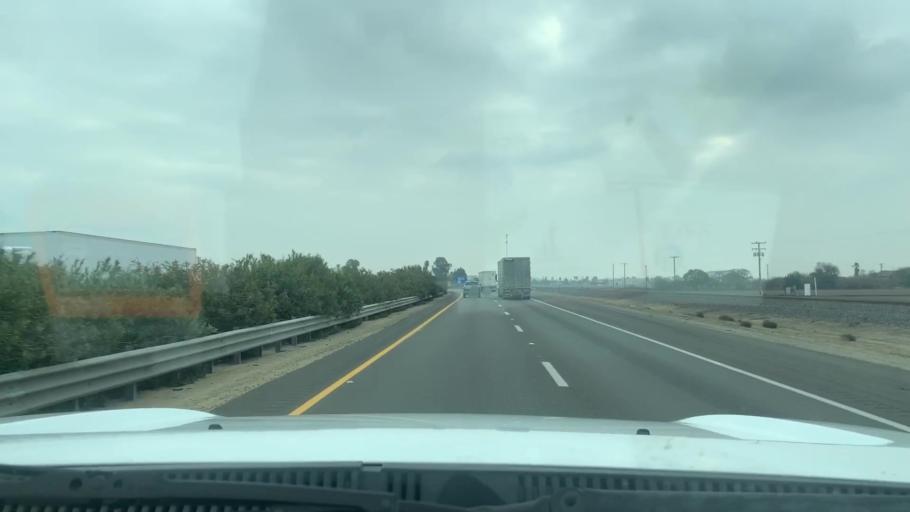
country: US
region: California
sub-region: Tulare County
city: Tipton
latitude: 36.0746
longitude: -119.3179
